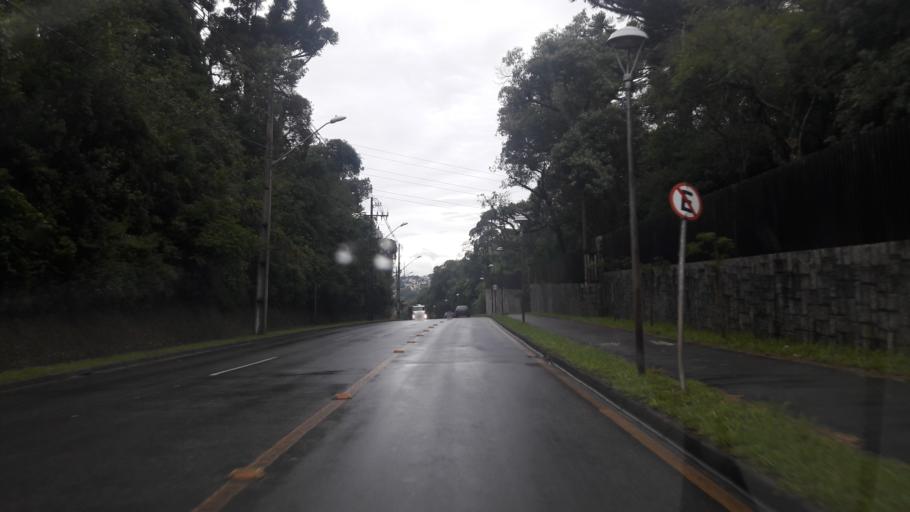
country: BR
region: Parana
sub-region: Curitiba
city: Curitiba
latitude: -25.3838
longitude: -49.3099
